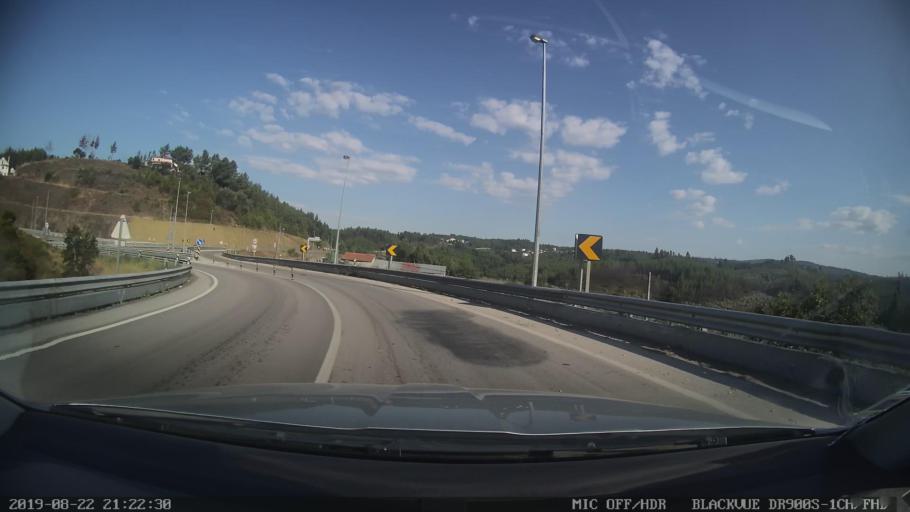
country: PT
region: Castelo Branco
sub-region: Serta
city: Serta
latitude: 39.8214
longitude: -8.1008
